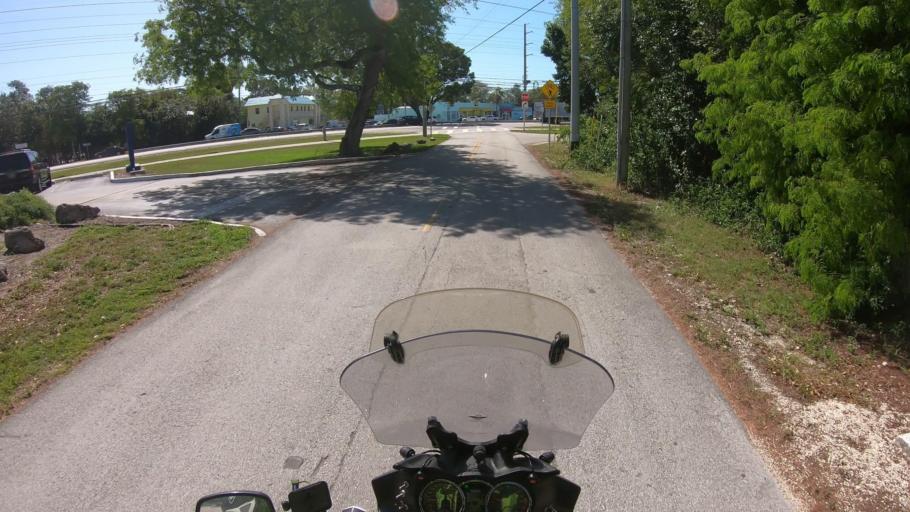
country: US
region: Florida
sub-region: Monroe County
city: Key Largo
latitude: 25.1002
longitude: -80.4355
